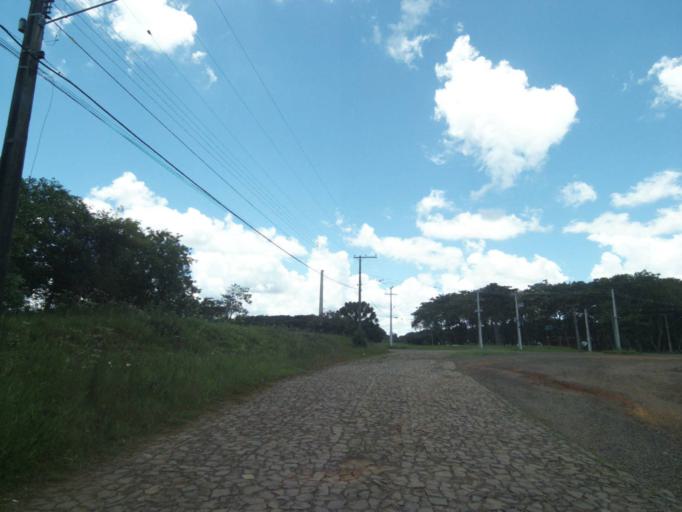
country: BR
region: Parana
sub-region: Pinhao
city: Pinhao
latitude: -25.7912
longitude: -52.0837
